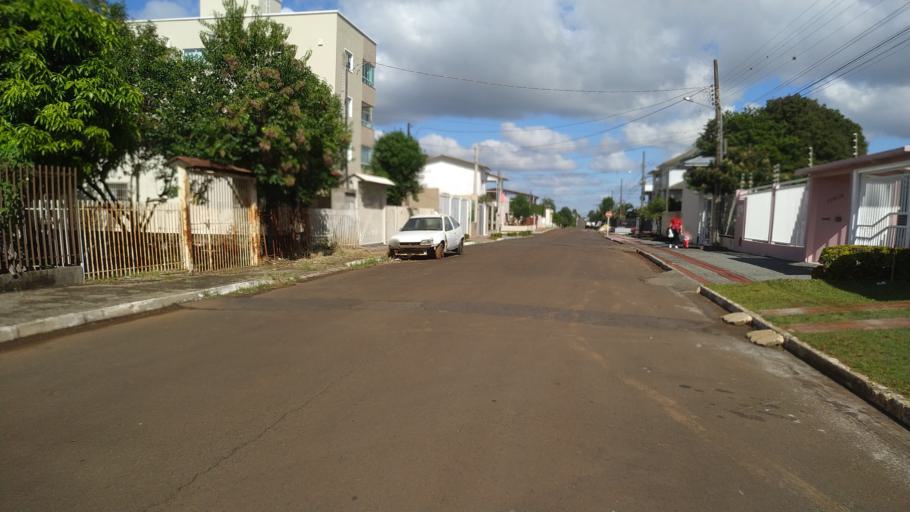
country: BR
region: Santa Catarina
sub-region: Chapeco
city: Chapeco
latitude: -27.0976
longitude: -52.6334
